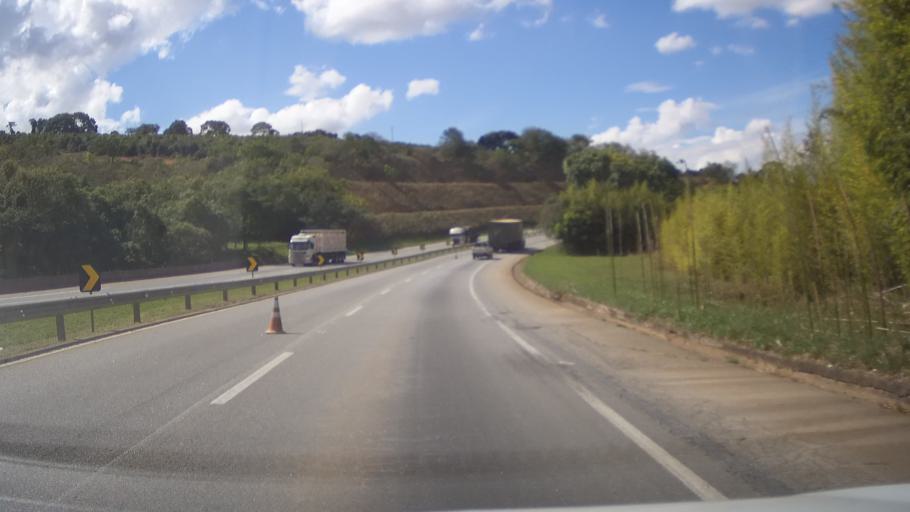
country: BR
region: Minas Gerais
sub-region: Oliveira
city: Oliveira
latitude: -20.8351
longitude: -44.8247
